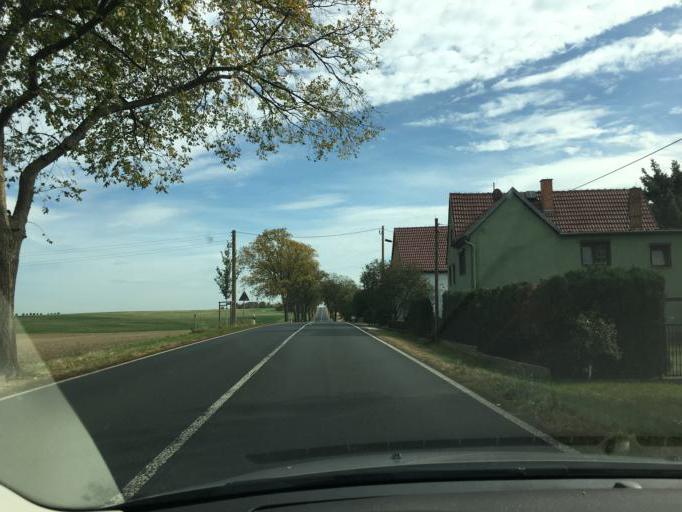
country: DE
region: Saxony
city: Lommatzsch
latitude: 51.2283
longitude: 13.3376
